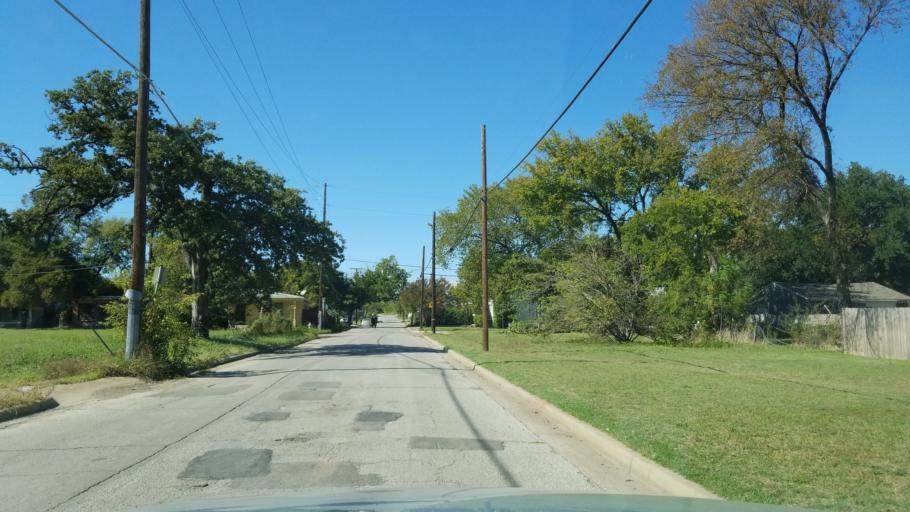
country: US
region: Texas
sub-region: Dallas County
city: Dallas
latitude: 32.7757
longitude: -96.7455
